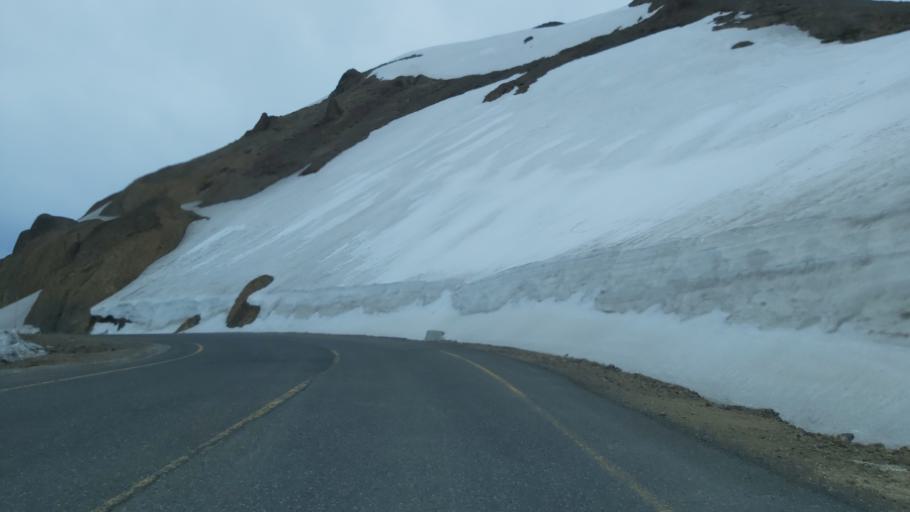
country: CL
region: Maule
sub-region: Provincia de Linares
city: Colbun
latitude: -36.0148
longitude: -70.5152
